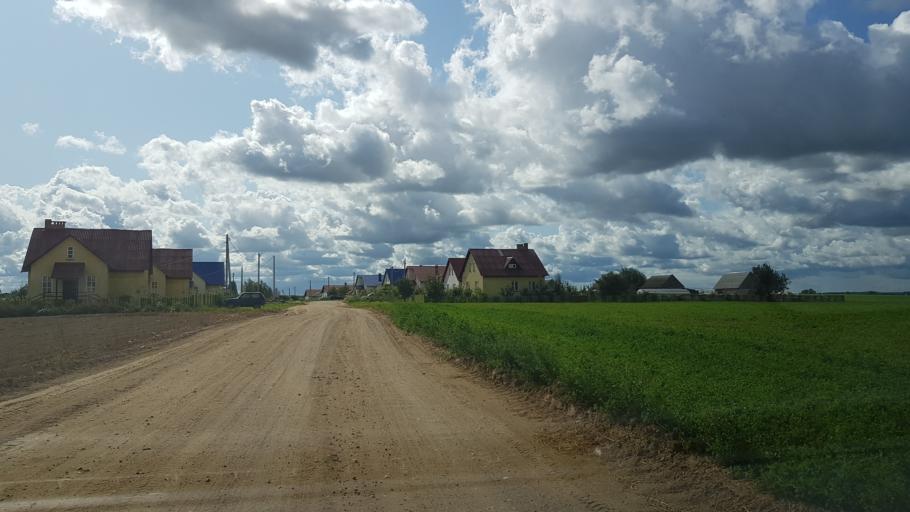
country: BY
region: Minsk
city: Dzyarzhynsk
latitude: 53.7473
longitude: 27.2122
